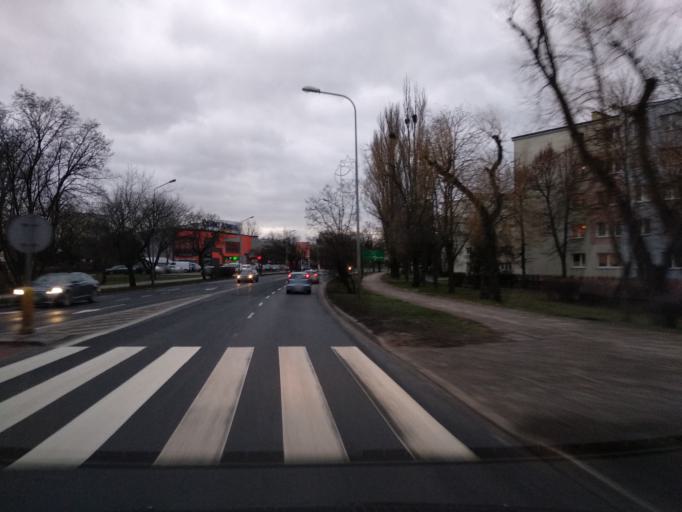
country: PL
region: Greater Poland Voivodeship
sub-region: Konin
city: Konin
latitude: 52.2298
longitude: 18.2660
